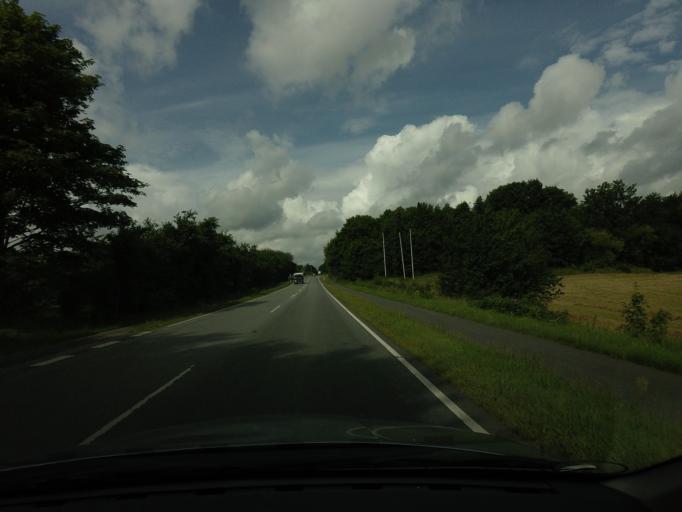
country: DK
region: North Denmark
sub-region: Hjorring Kommune
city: Tars
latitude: 57.3824
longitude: 10.1286
